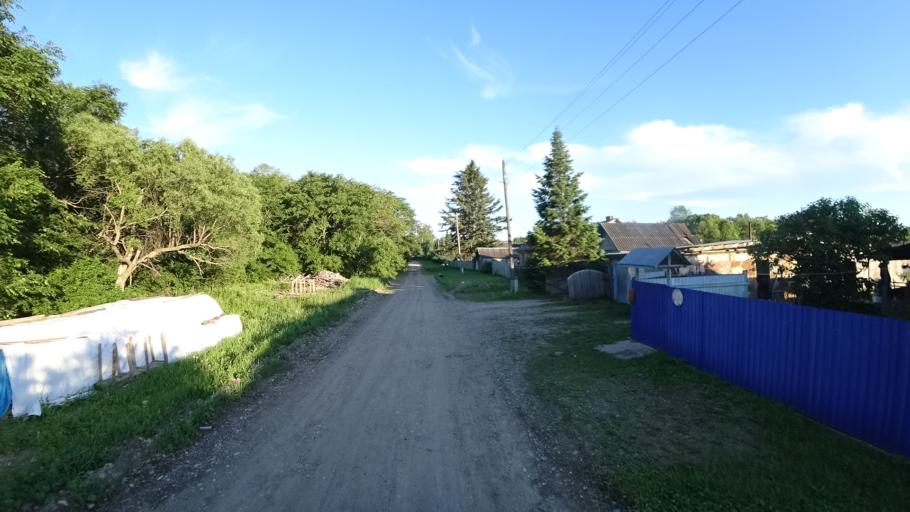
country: RU
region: Khabarovsk Krai
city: Khor
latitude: 47.8561
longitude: 135.0020
